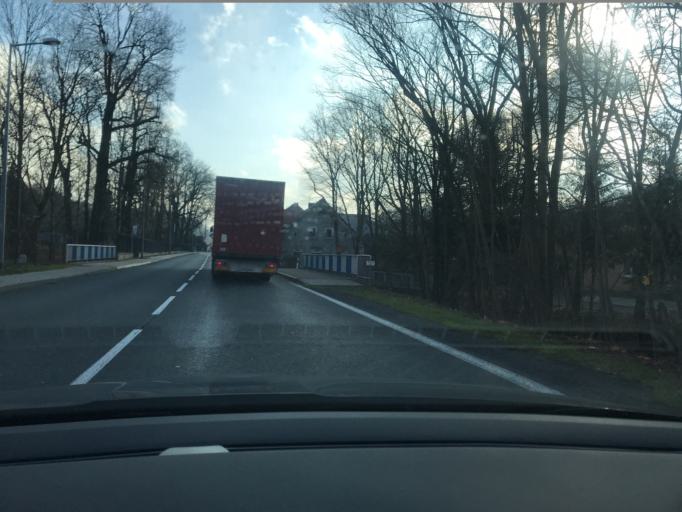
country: PL
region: Lower Silesian Voivodeship
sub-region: Powiat klodzki
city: Kudowa-Zdroj
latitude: 50.4231
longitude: 16.2575
